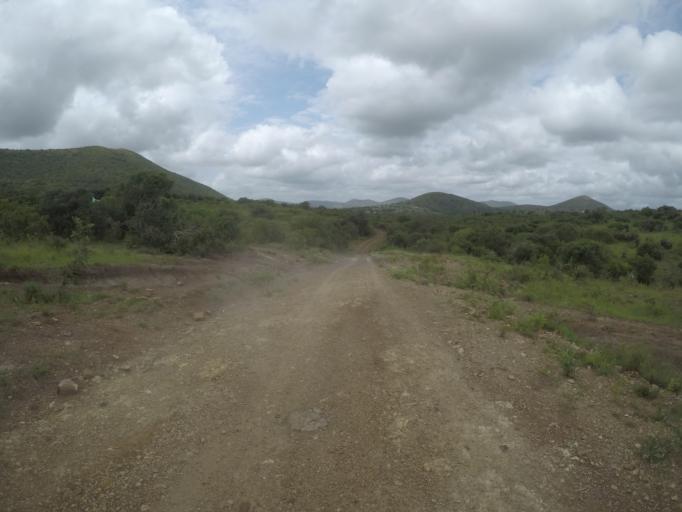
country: ZA
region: KwaZulu-Natal
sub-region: uThungulu District Municipality
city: Empangeni
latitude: -28.5832
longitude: 31.8679
